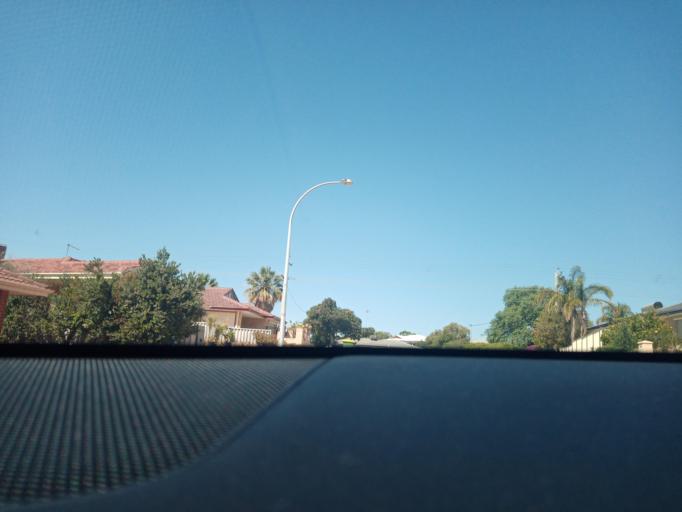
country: AU
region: Western Australia
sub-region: City of Cockburn
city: Coogee
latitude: -32.1244
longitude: 115.7840
